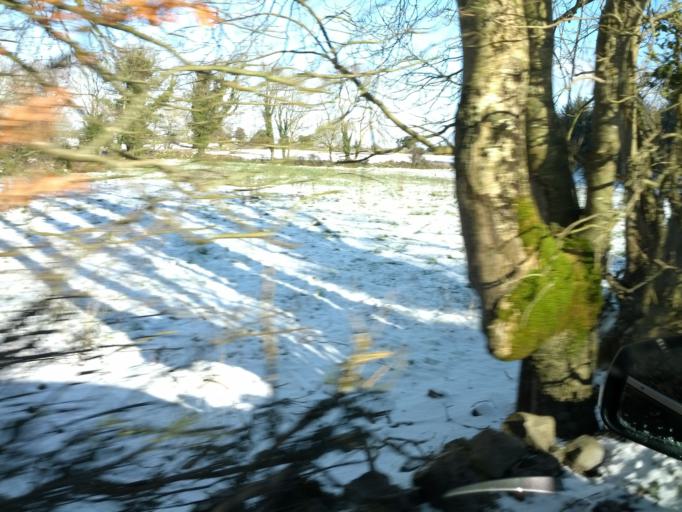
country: IE
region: Connaught
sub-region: County Galway
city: Athenry
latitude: 53.1981
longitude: -8.7996
